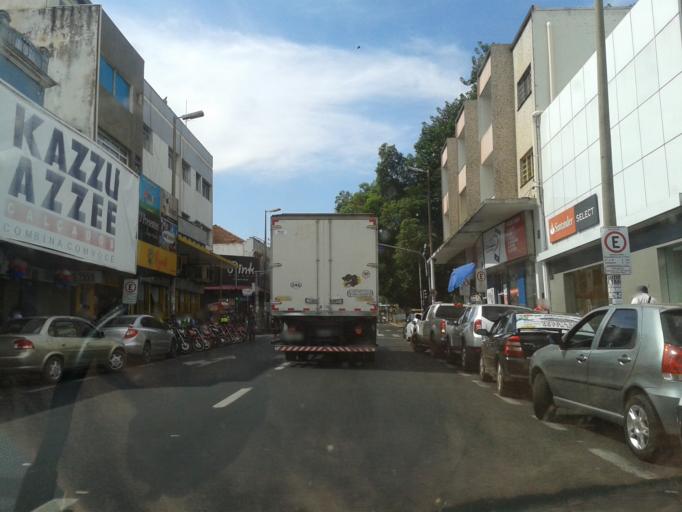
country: BR
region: Minas Gerais
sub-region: Uberlandia
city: Uberlandia
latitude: -18.9163
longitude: -48.2763
